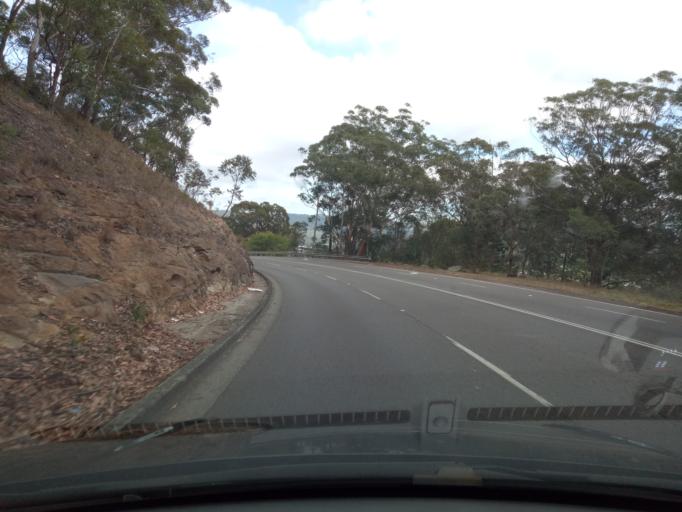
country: AU
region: New South Wales
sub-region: Gosford Shire
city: Gosford
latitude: -33.4225
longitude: 151.3457
